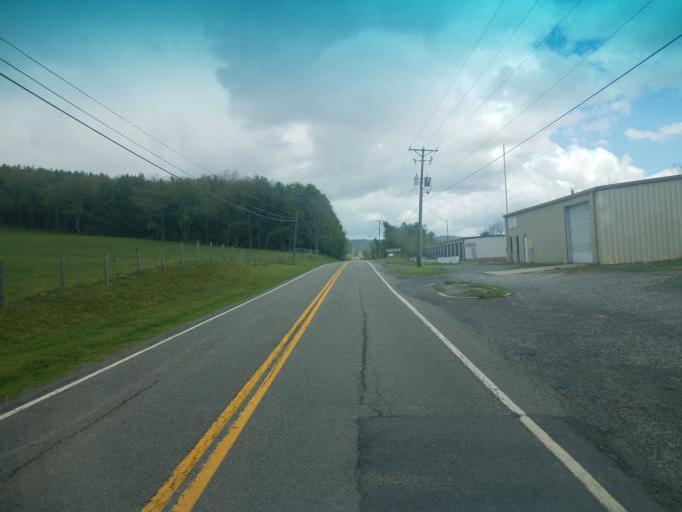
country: US
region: Virginia
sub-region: Bland County
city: Bland
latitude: 37.0891
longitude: -81.1405
